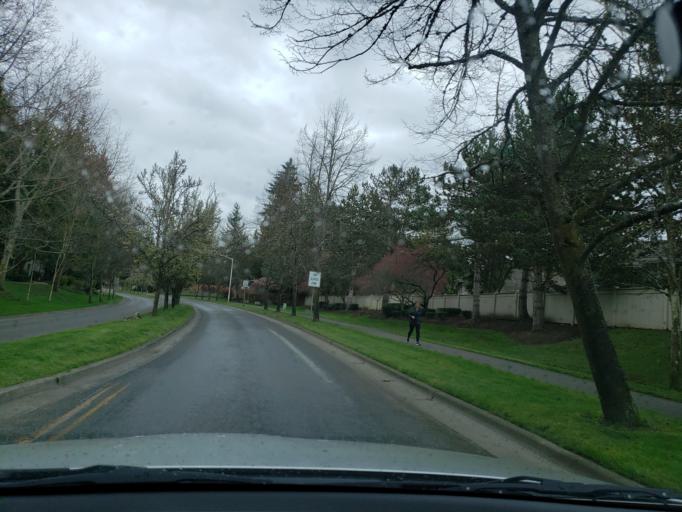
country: US
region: Washington
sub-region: Snohomish County
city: Meadowdale
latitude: 47.8862
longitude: -122.3076
